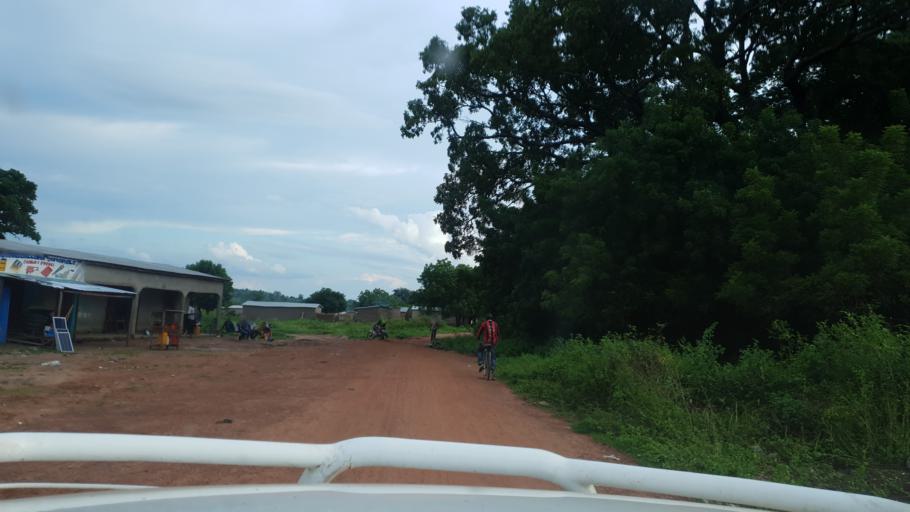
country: CI
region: Savanes
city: Tengrela
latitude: 10.5454
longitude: -6.9169
